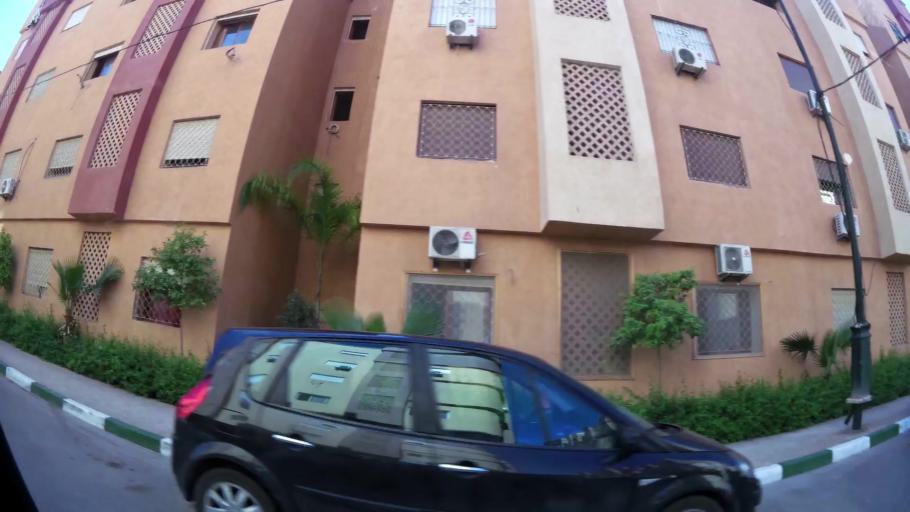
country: MA
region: Marrakech-Tensift-Al Haouz
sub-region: Marrakech
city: Marrakesh
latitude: 31.6600
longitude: -8.0208
